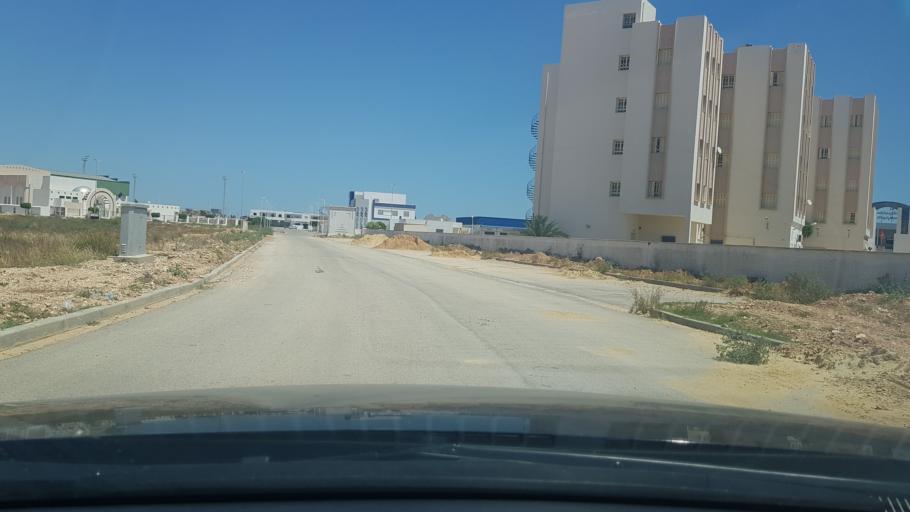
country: TN
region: Safaqis
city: Al Qarmadah
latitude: 34.8405
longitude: 10.7550
